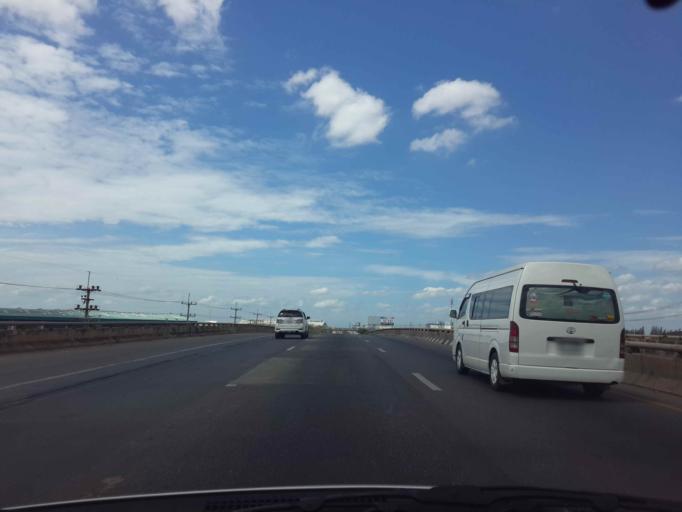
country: TH
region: Samut Sakhon
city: Ban Phaeo
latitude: 13.4853
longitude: 100.1205
